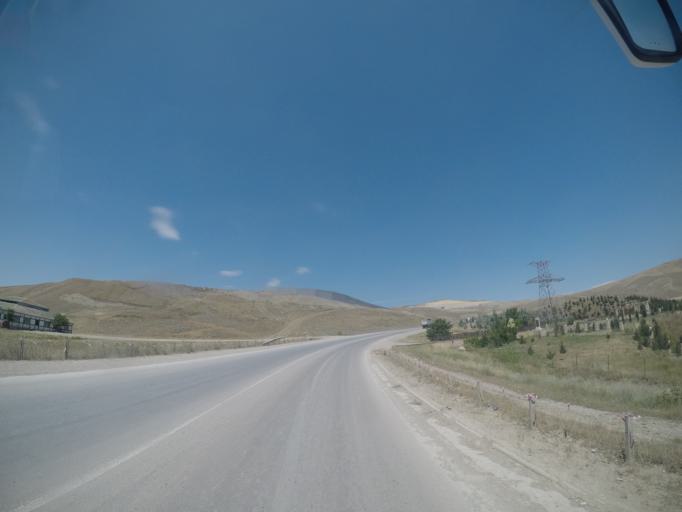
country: AZ
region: Samaxi
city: Shamakhi
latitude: 40.5571
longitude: 48.7566
